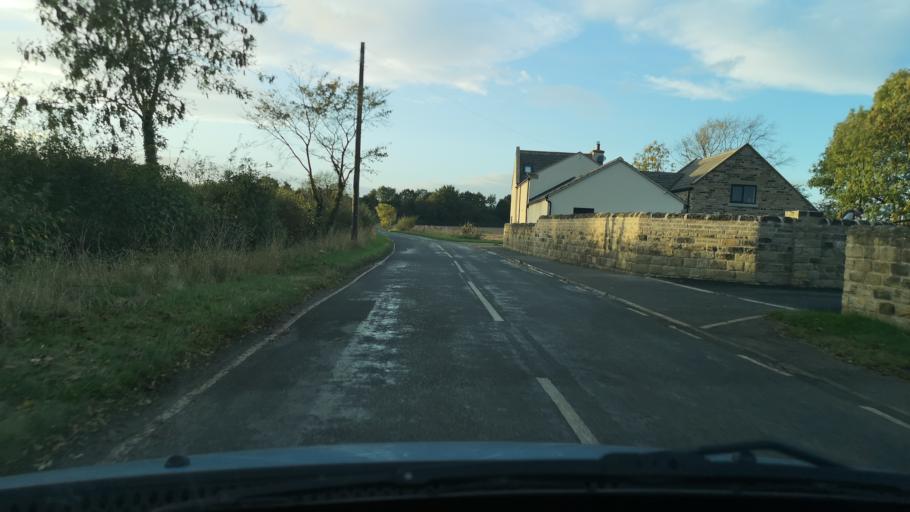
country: GB
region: England
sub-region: City and Borough of Wakefield
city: Low Ackworth
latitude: 53.6496
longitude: -1.3100
